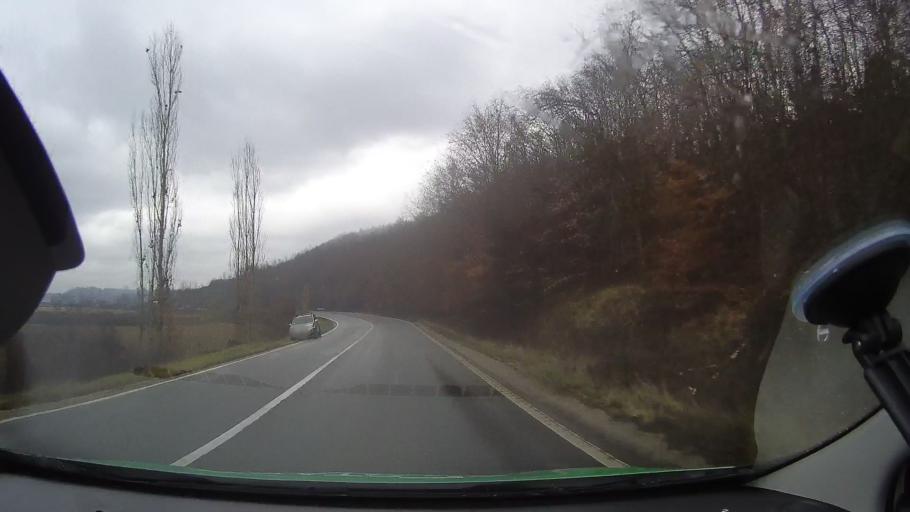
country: RO
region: Arad
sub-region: Comuna Almas
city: Almas
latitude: 46.2969
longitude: 22.2036
